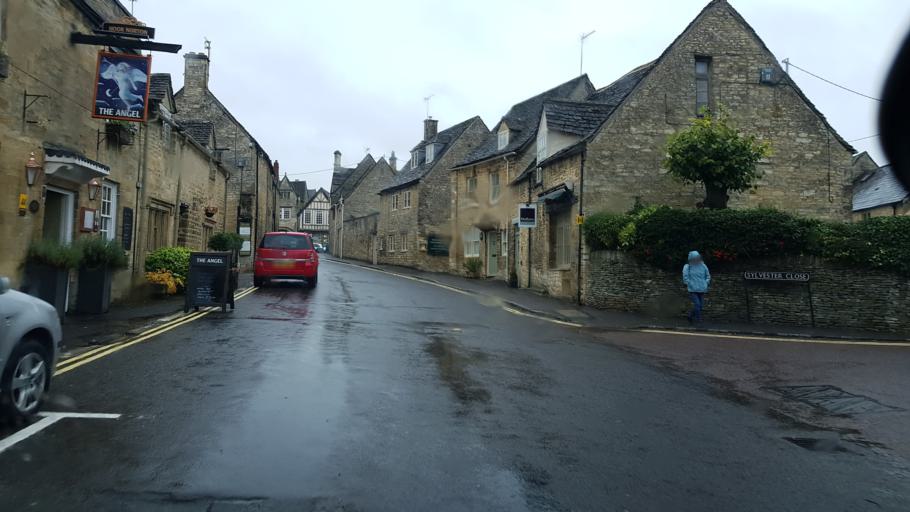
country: GB
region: England
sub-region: Oxfordshire
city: Burford
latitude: 51.8076
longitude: -1.6353
